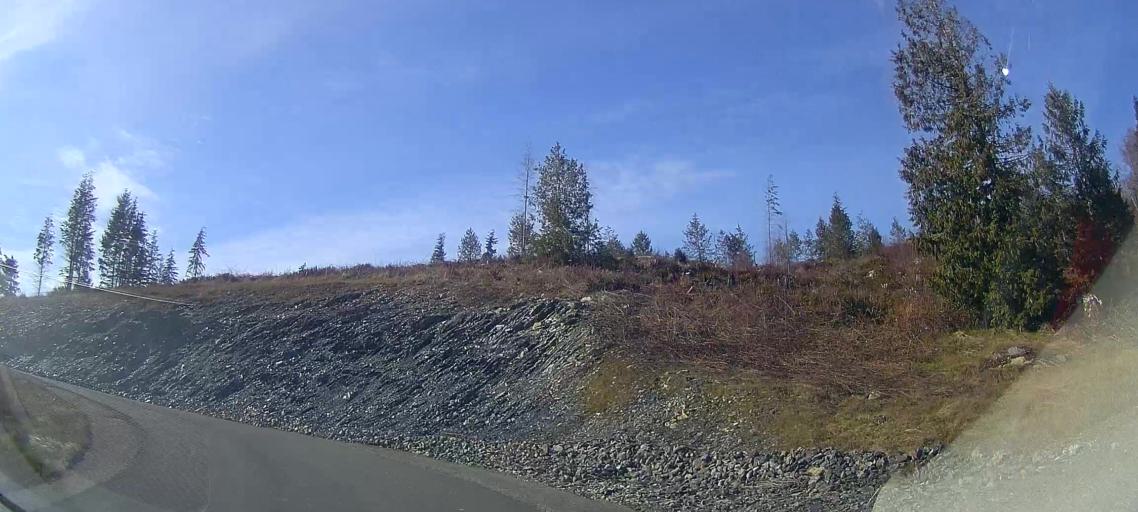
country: US
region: Washington
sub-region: Whatcom County
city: Sudden Valley
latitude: 48.5983
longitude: -122.3854
